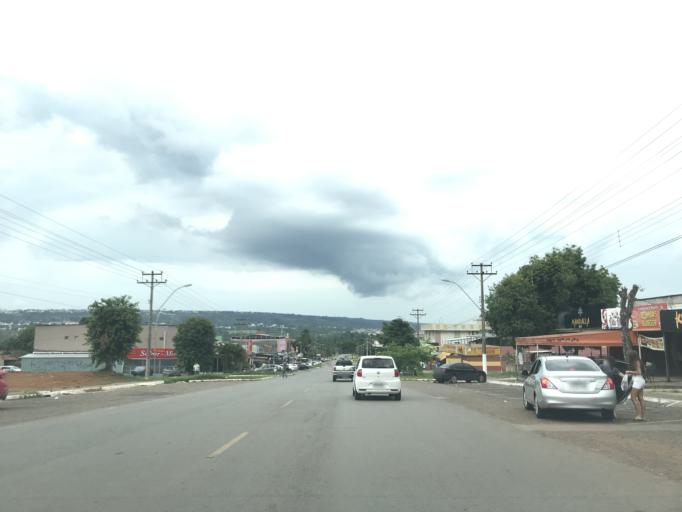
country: BR
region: Federal District
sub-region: Brasilia
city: Brasilia
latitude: -15.6564
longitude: -47.8064
